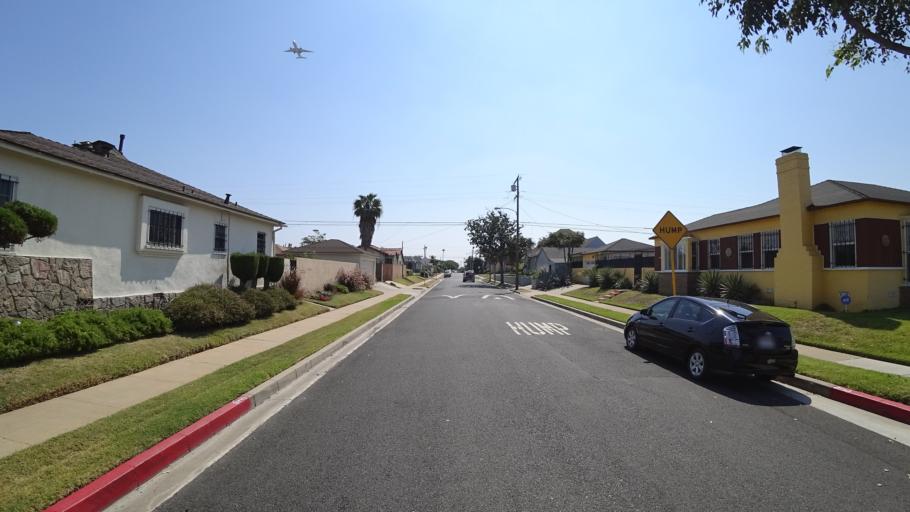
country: US
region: California
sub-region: Los Angeles County
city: Westmont
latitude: 33.9581
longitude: -118.3242
